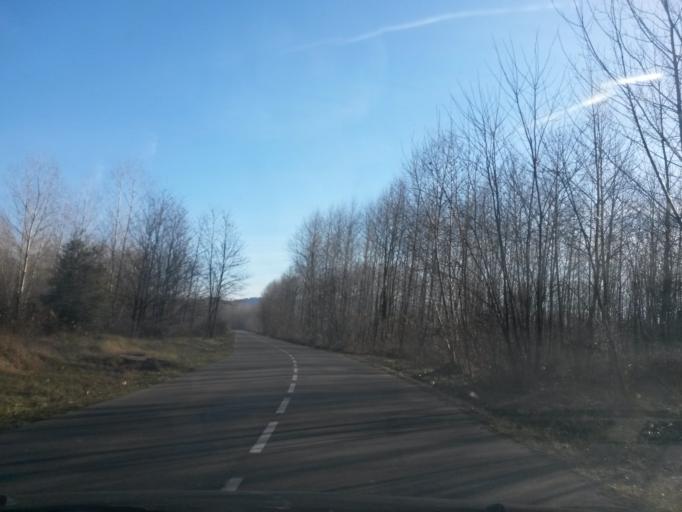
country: ES
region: Catalonia
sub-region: Provincia de Girona
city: Angles
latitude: 41.9634
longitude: 2.6534
